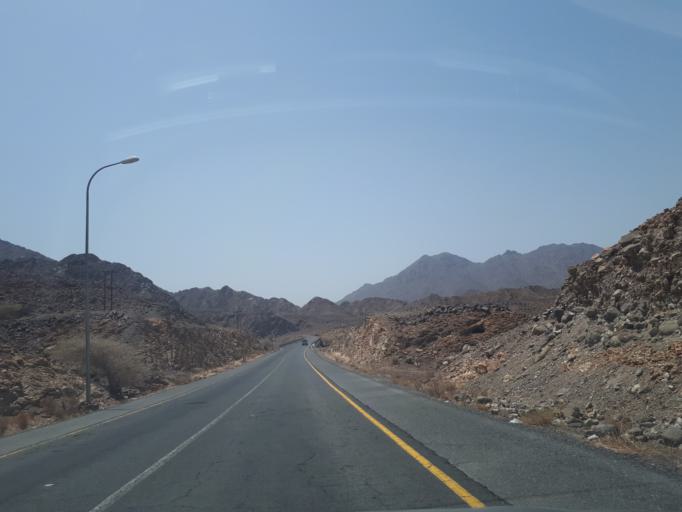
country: OM
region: Muhafazat ad Dakhiliyah
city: Sufalat Sama'il
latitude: 23.1846
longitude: 58.0965
